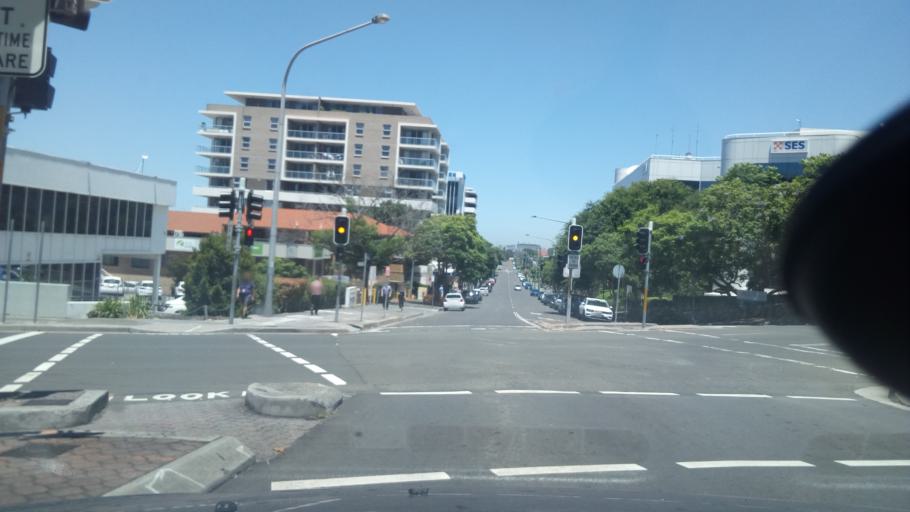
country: AU
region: New South Wales
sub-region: Wollongong
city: Wollongong
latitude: -34.4259
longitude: 150.8909
